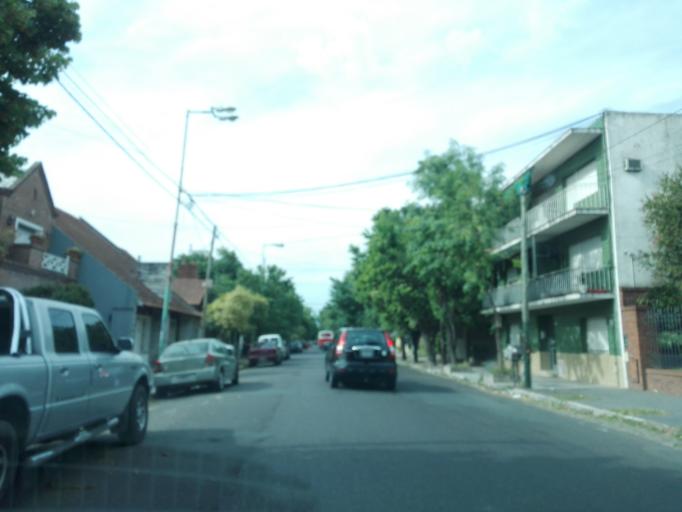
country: AR
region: Buenos Aires
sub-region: Partido de Lomas de Zamora
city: Lomas de Zamora
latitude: -34.7472
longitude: -58.3968
